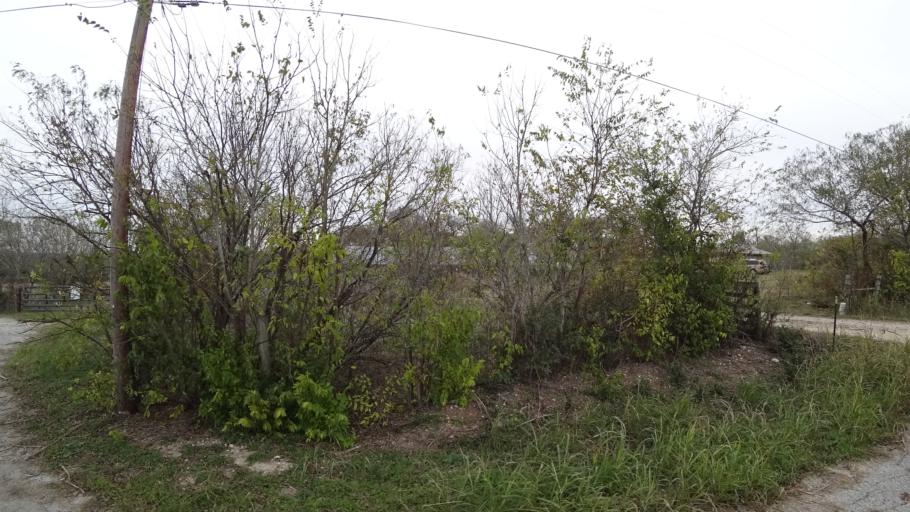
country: US
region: Texas
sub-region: Travis County
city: Garfield
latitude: 30.1222
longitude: -97.5608
